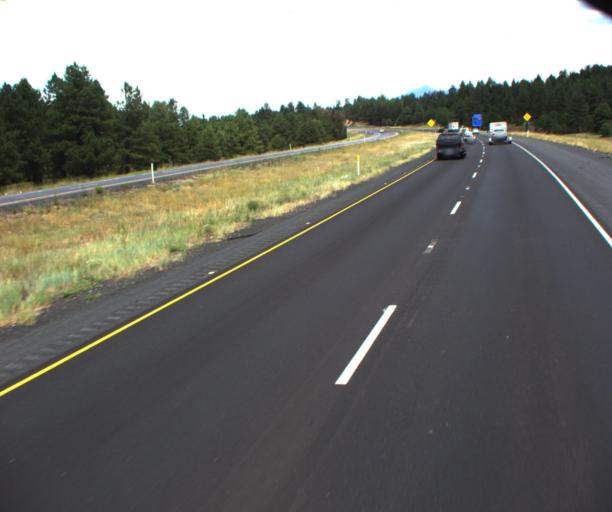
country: US
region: Arizona
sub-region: Coconino County
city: Kachina Village
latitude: 35.1176
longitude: -111.6803
